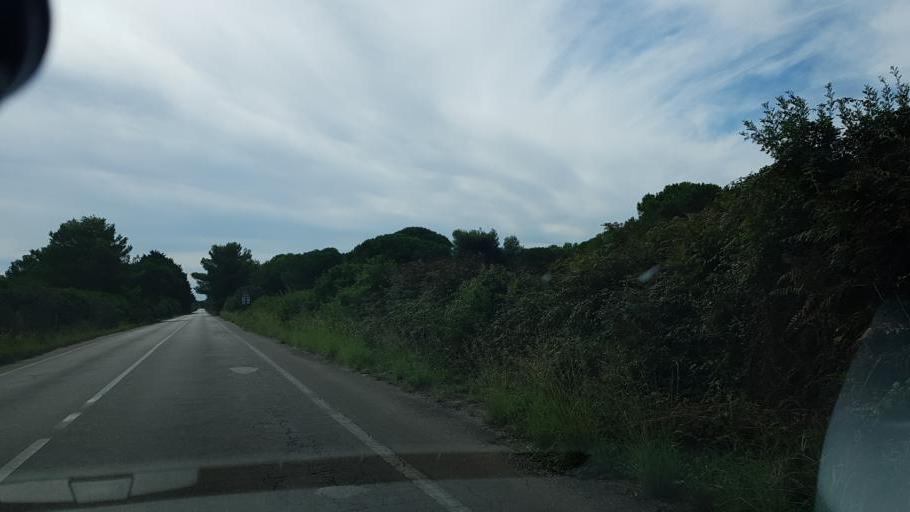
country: IT
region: Apulia
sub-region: Provincia di Lecce
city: Borgagne
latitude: 40.2495
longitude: 18.4404
